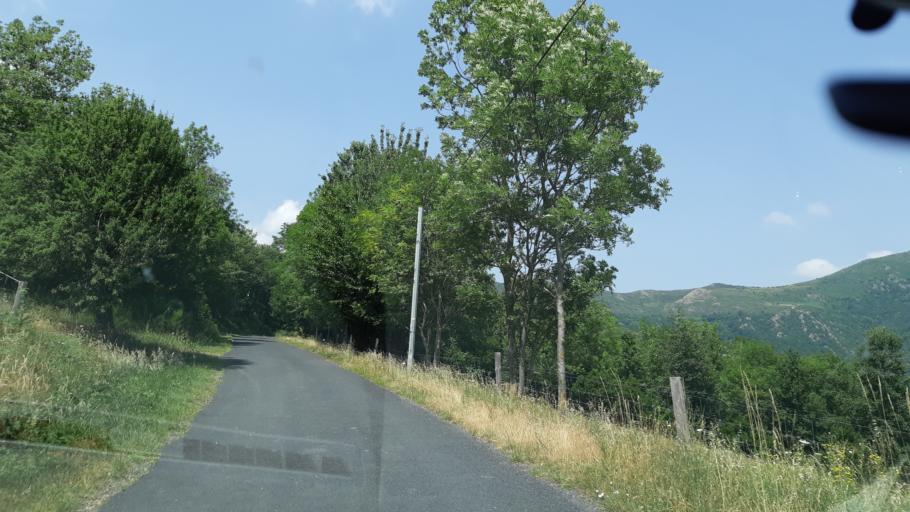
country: FR
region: Languedoc-Roussillon
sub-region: Departement des Pyrenees-Orientales
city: Arles
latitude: 42.5482
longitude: 2.5843
